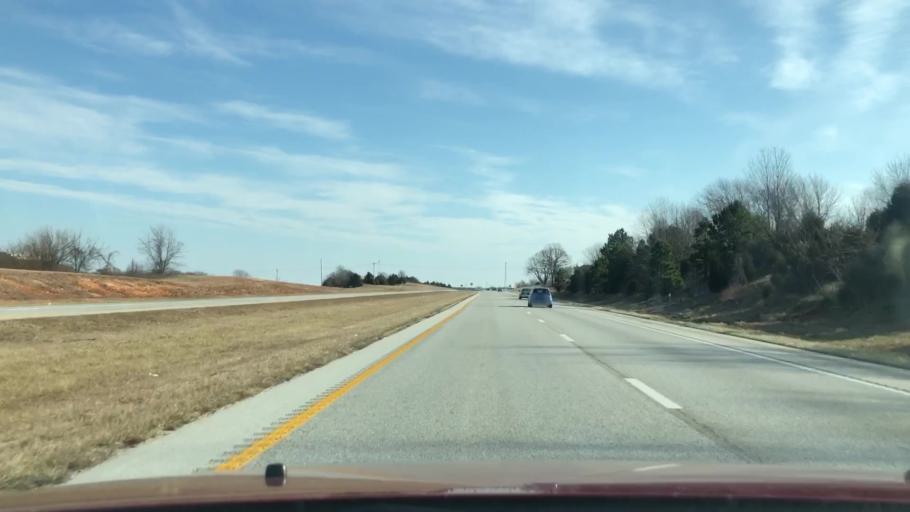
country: US
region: Missouri
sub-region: Webster County
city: Seymour
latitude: 37.1564
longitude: -92.7765
